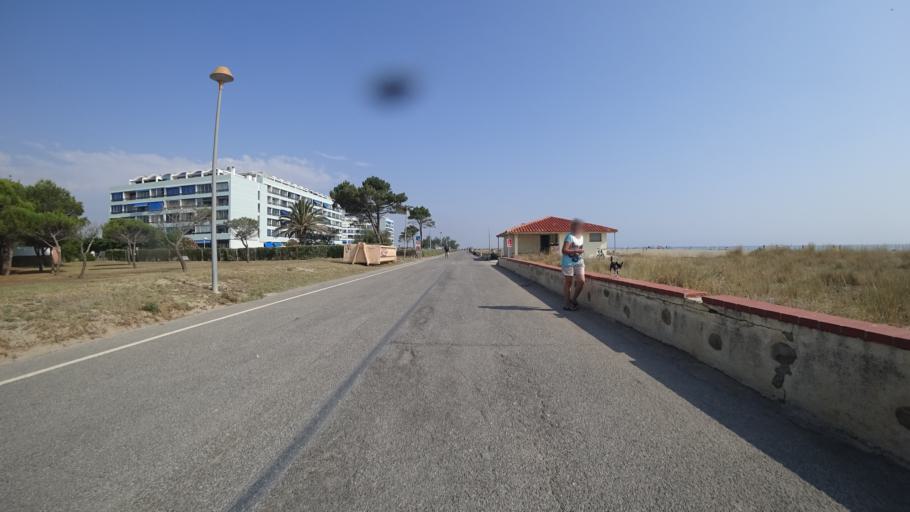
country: FR
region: Languedoc-Roussillon
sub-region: Departement des Pyrenees-Orientales
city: Saint-Cyprien-Plage
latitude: 42.6376
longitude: 3.0344
